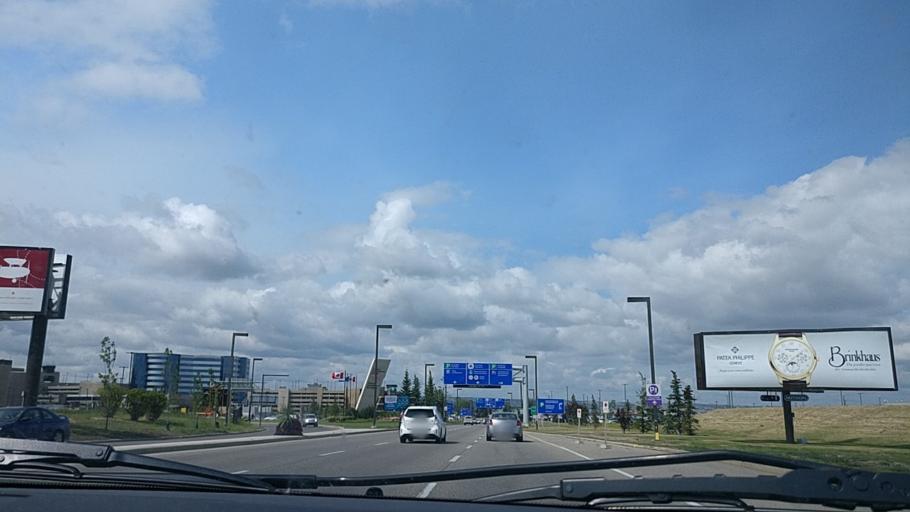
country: CA
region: Alberta
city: Calgary
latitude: 51.1343
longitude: -114.0017
